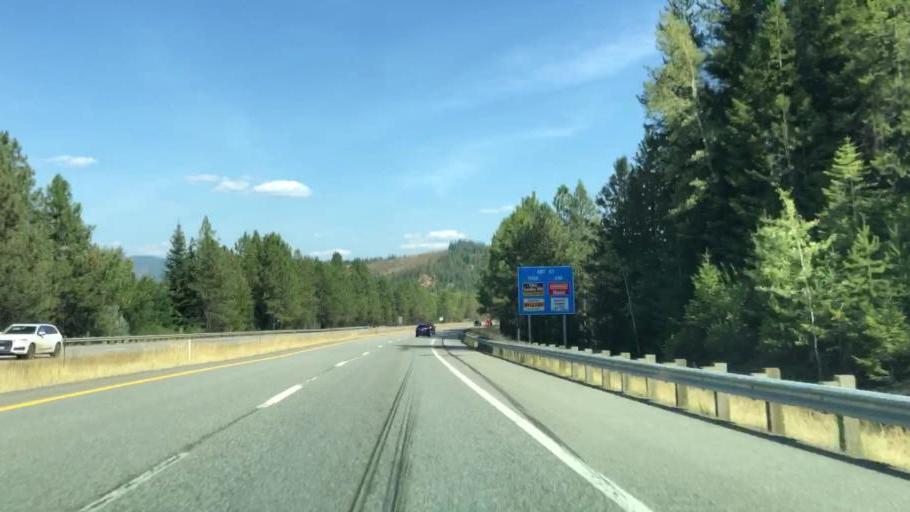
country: US
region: Idaho
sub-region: Shoshone County
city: Pinehurst
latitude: 47.5521
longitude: -116.2844
